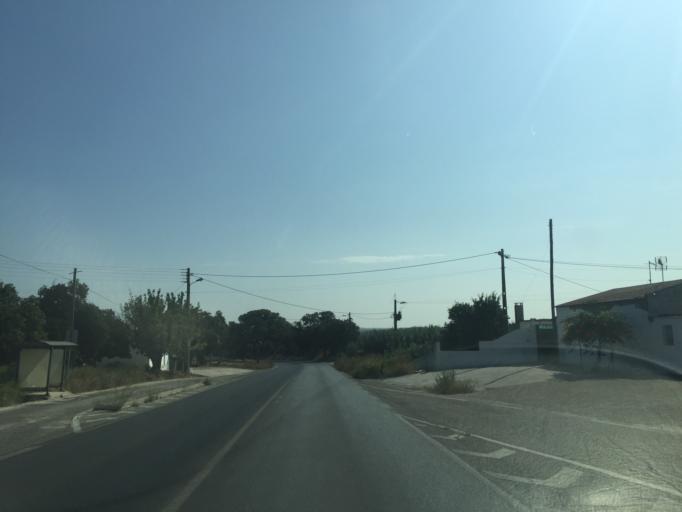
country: PT
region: Santarem
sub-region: Salvaterra de Magos
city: Salvaterra de Magos
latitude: 39.0301
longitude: -8.7464
